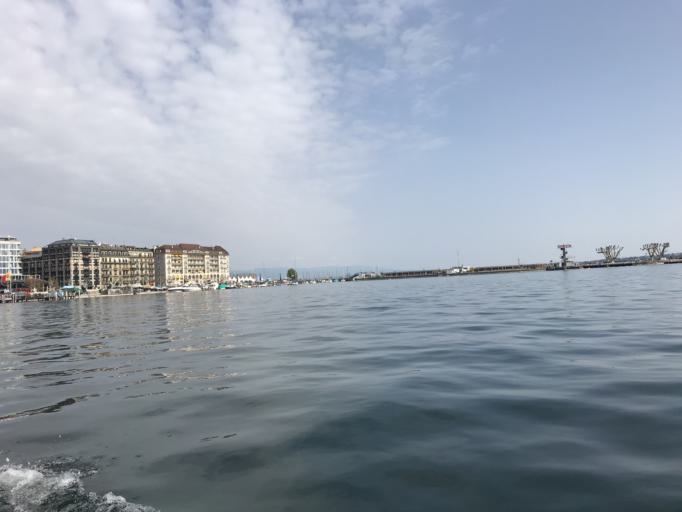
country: CH
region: Geneva
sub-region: Geneva
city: Geneve
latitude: 46.2077
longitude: 6.1522
